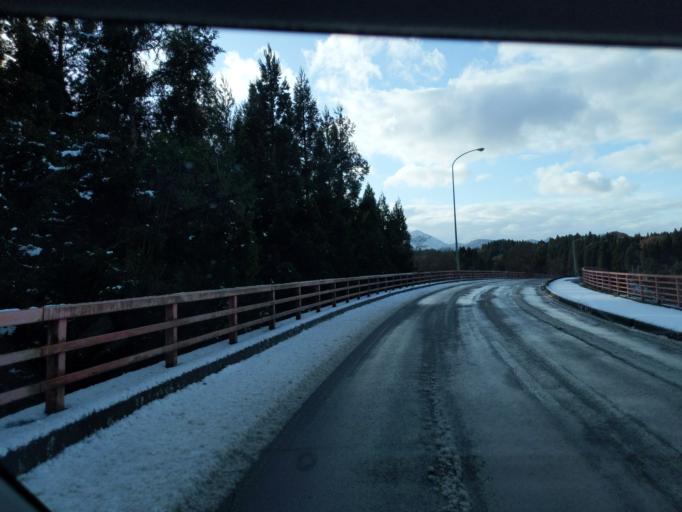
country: JP
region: Iwate
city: Kitakami
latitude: 39.2534
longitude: 141.0245
